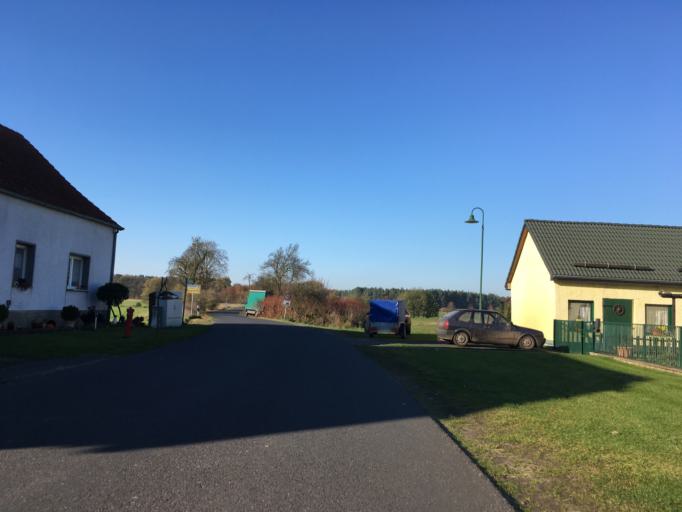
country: DE
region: Brandenburg
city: Spreenhagen
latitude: 52.3378
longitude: 13.9461
